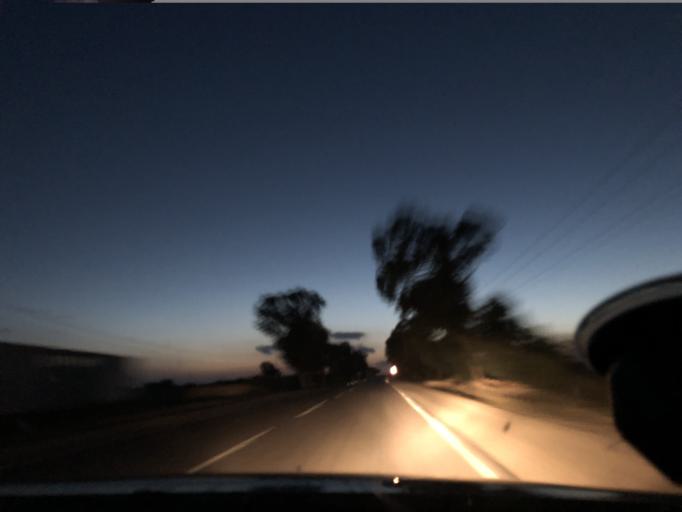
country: TN
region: Al Qasrayn
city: Kasserine
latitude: 35.2517
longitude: 9.0091
